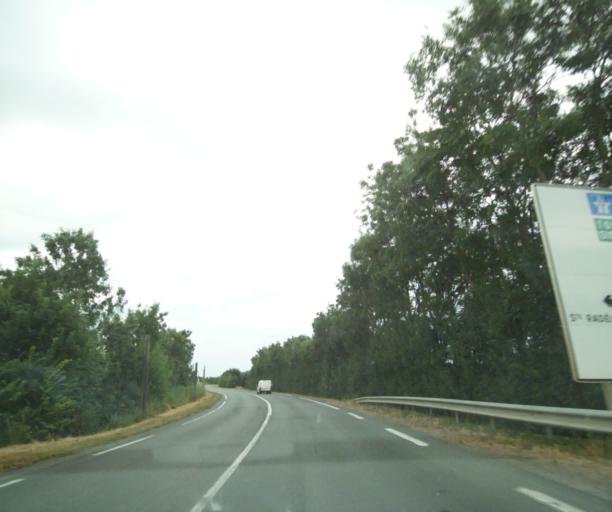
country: FR
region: Pays de la Loire
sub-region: Departement de la Vendee
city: Chaille-les-Marais
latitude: 46.4068
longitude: -1.0359
